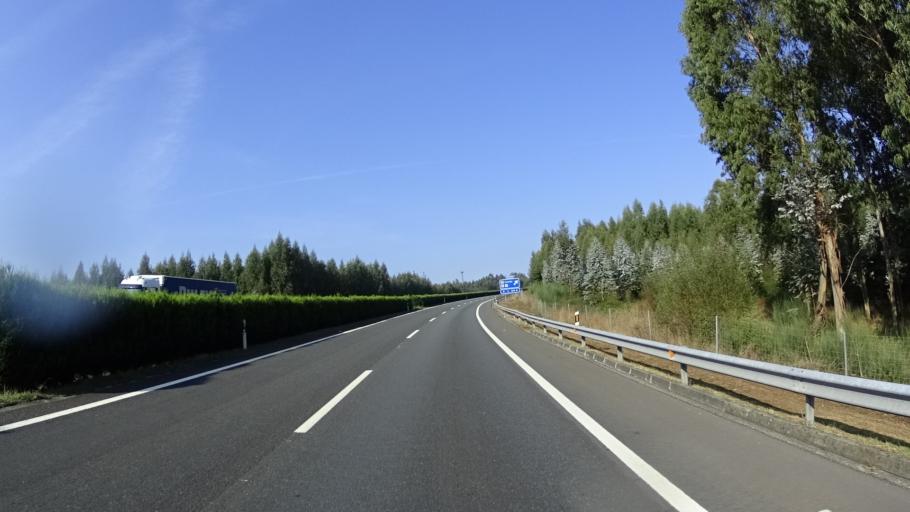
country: ES
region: Galicia
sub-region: Provincia da Coruna
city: Coiros
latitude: 43.2390
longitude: -8.1192
